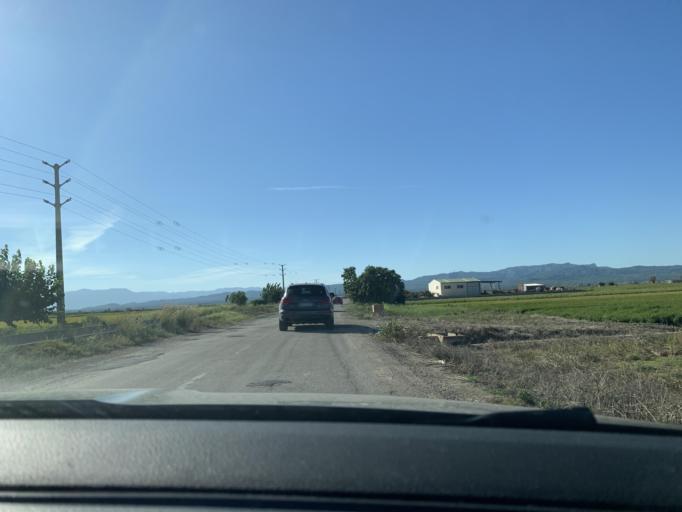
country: ES
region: Catalonia
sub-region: Provincia de Tarragona
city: Deltebre
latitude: 40.7488
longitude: 0.7268
